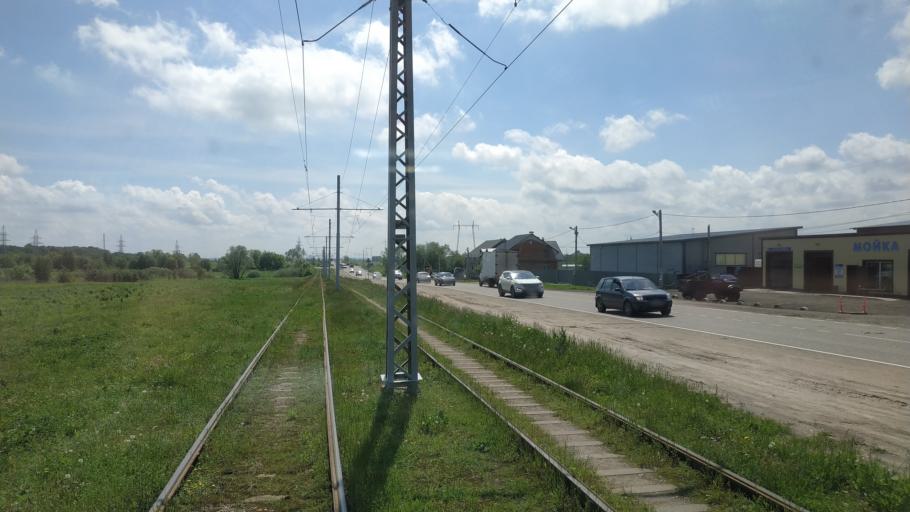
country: RU
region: Moskovskaya
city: Sychevo
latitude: 55.0625
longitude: 38.7259
